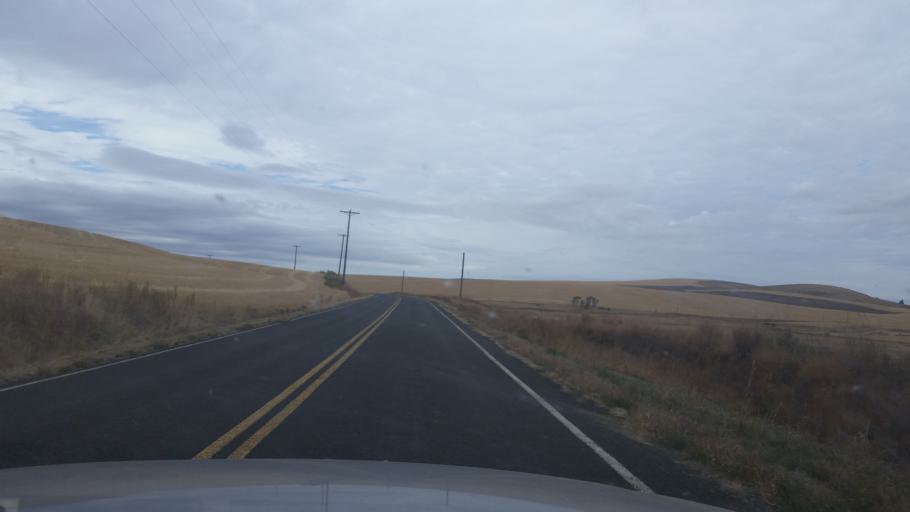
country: US
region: Washington
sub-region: Spokane County
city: Medical Lake
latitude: 47.5226
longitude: -117.9111
